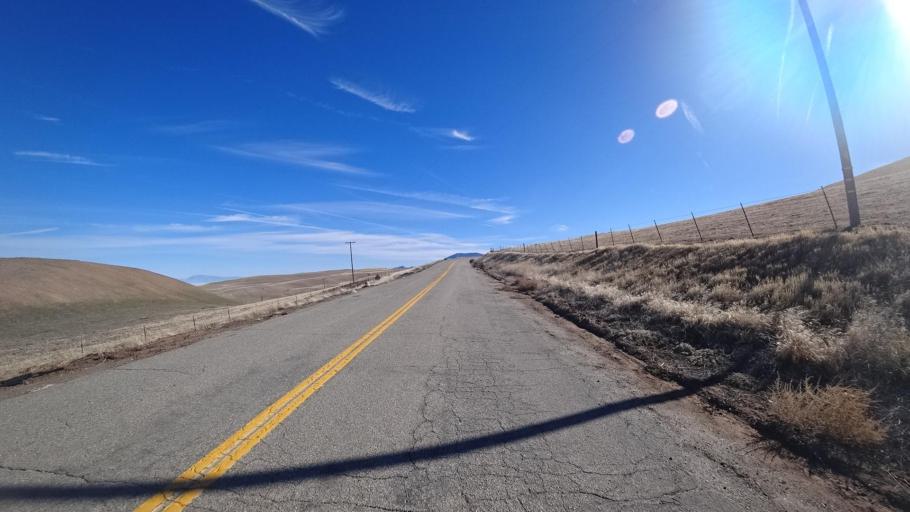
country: US
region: California
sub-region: Kern County
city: Maricopa
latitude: 34.9306
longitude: -119.4113
